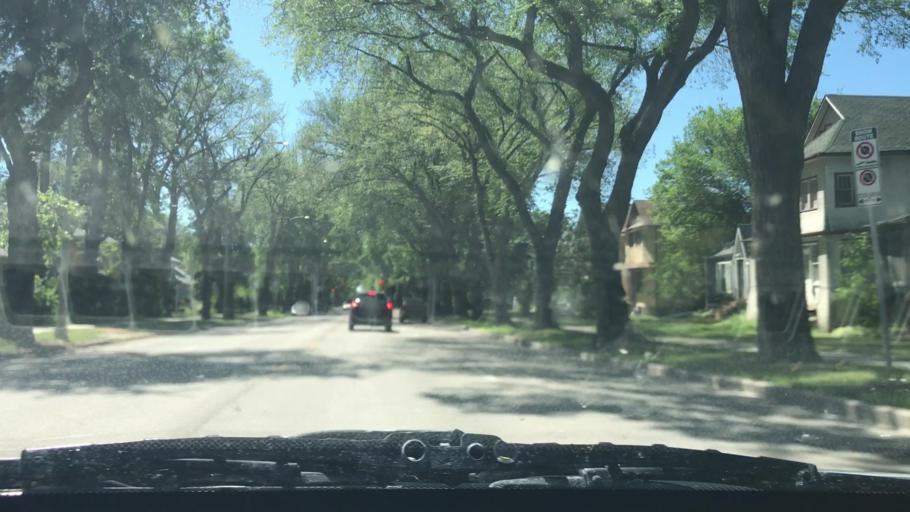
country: CA
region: Manitoba
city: Winnipeg
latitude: 49.8584
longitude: -97.1340
